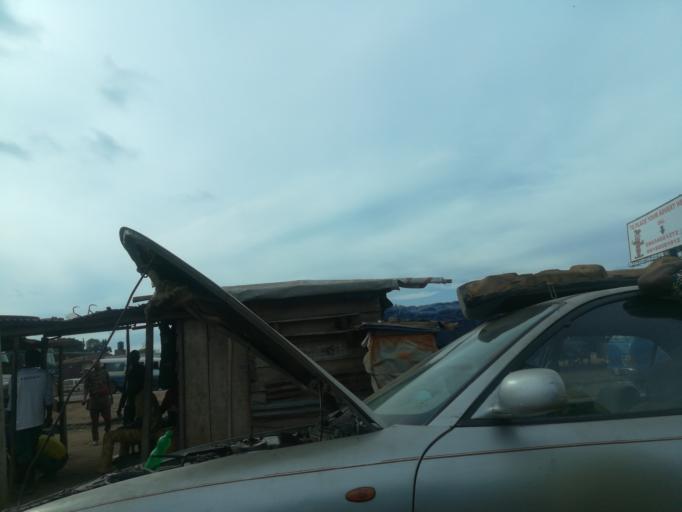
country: NG
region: Oyo
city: Ibadan
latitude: 7.3832
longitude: 3.9340
